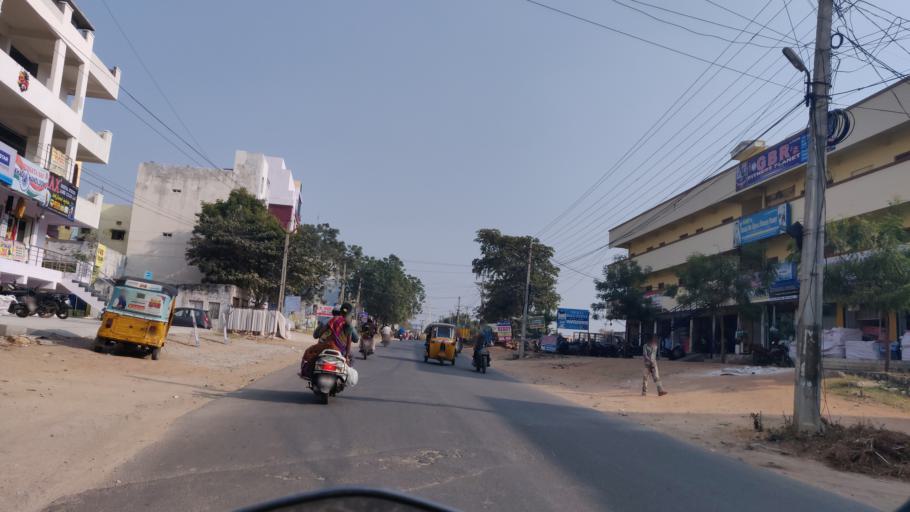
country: IN
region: Telangana
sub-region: Rangareddi
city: Uppal Kalan
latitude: 17.3986
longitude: 78.5863
